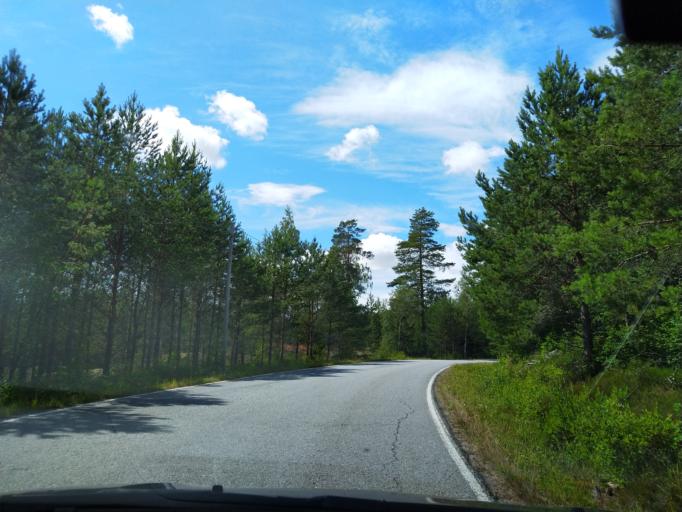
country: FI
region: Uusimaa
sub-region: Raaseporin
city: Karis
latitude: 59.9923
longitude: 23.6912
